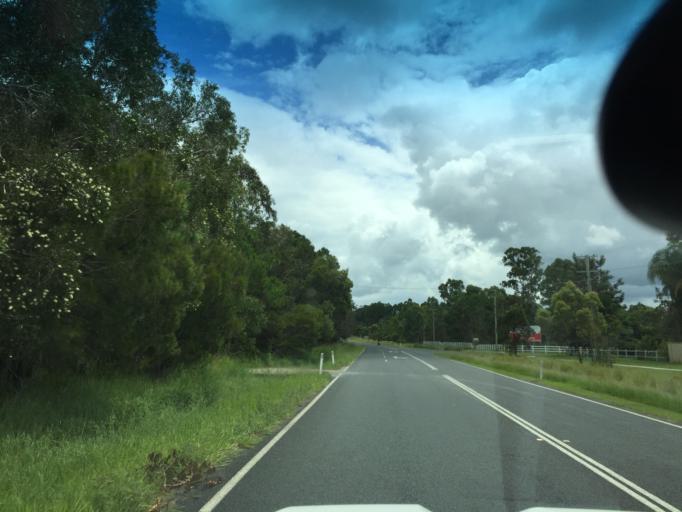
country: AU
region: Queensland
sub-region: Moreton Bay
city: Caboolture
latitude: -27.0519
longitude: 152.9382
